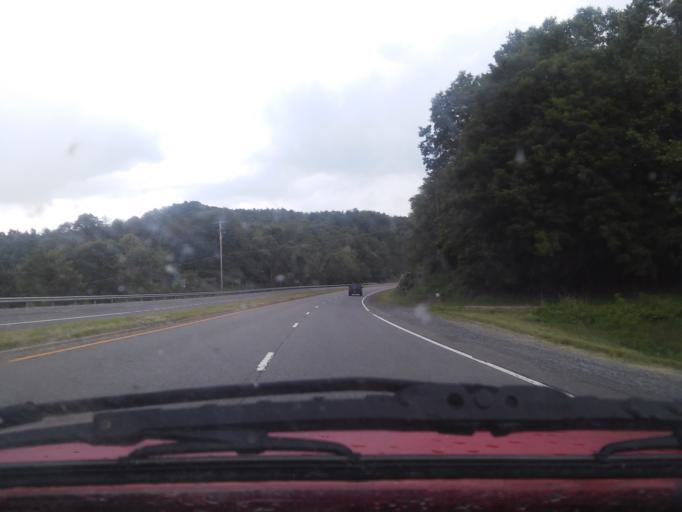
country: US
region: Virginia
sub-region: Montgomery County
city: Prices Fork
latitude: 37.3069
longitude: -80.5159
